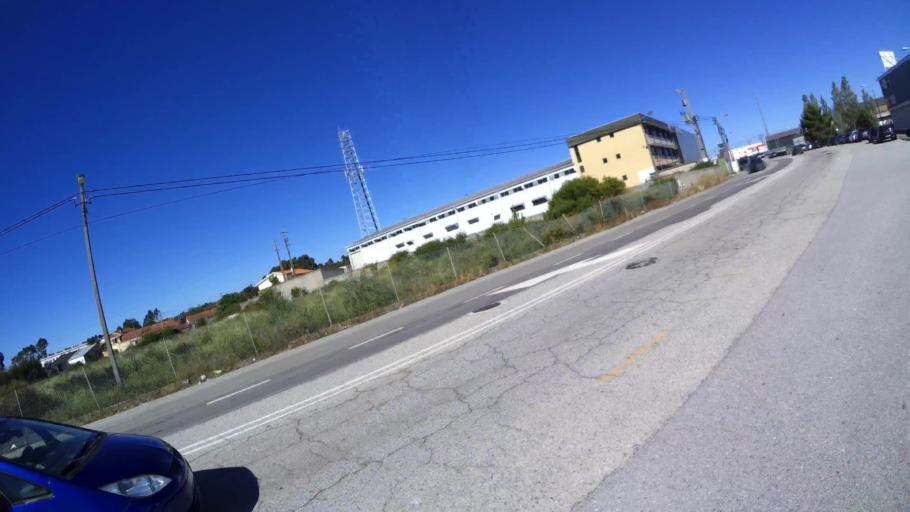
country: PT
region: Aveiro
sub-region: Aveiro
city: Aveiro
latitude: 40.6522
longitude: -8.6140
